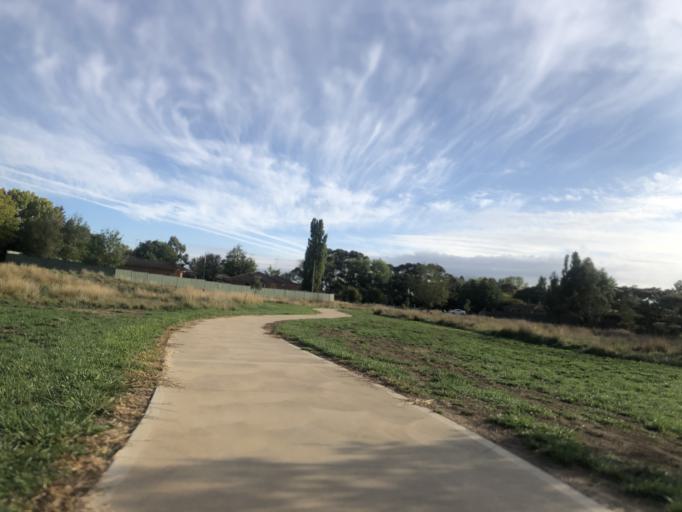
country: AU
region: New South Wales
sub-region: Orange Municipality
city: Orange
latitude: -33.2949
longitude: 149.0925
